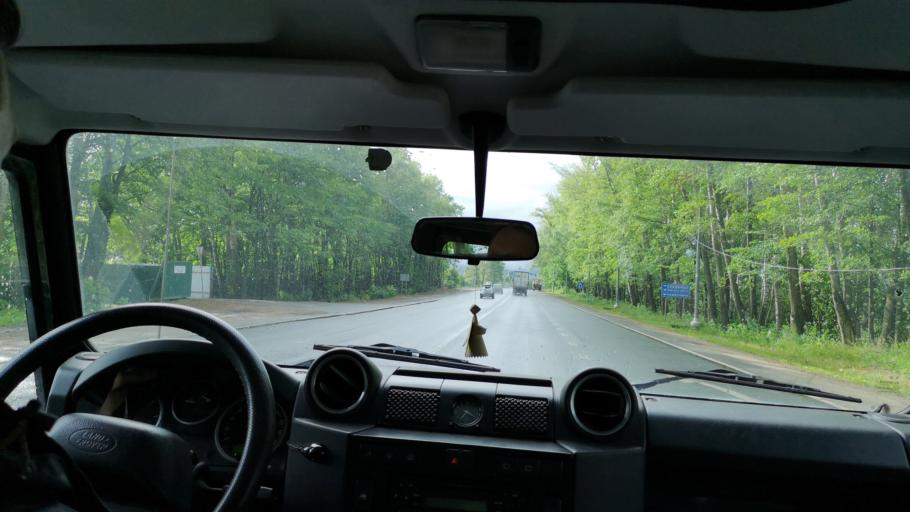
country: RU
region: Moskovskaya
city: Dmitrov
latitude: 56.3613
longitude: 37.4830
